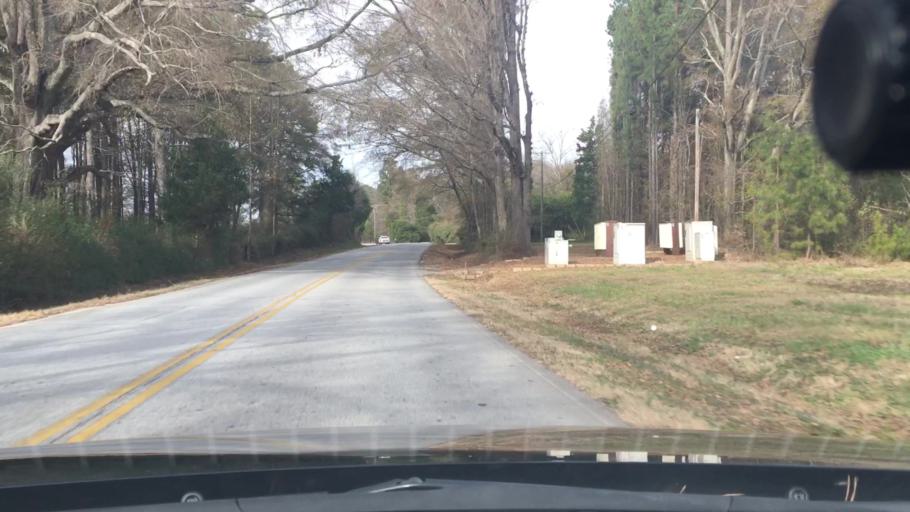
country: US
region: Georgia
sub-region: Coweta County
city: Senoia
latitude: 33.2973
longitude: -84.4609
